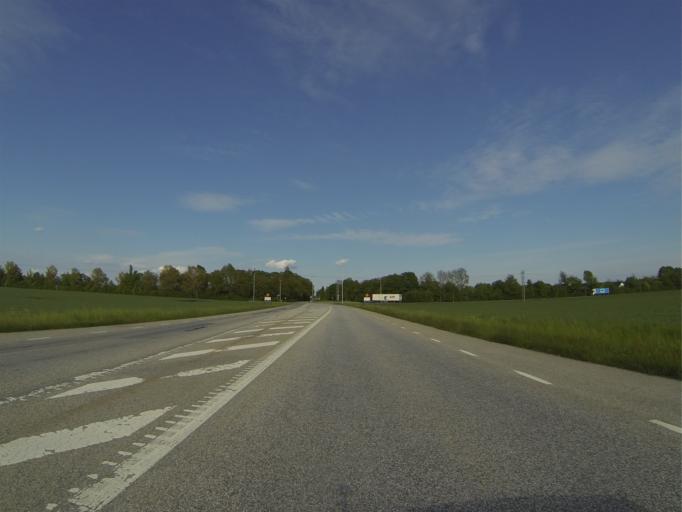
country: SE
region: Skane
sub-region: Staffanstorps Kommun
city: Staffanstorp
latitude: 55.6400
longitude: 13.1838
